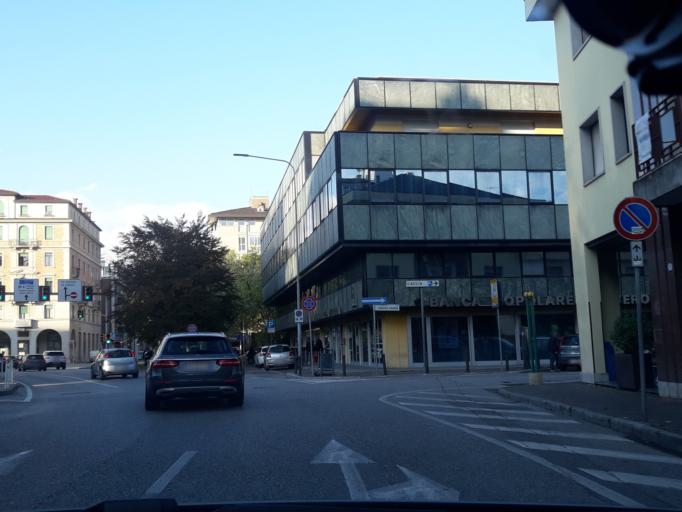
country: IT
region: Friuli Venezia Giulia
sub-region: Provincia di Udine
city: Udine
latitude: 46.0703
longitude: 13.2357
